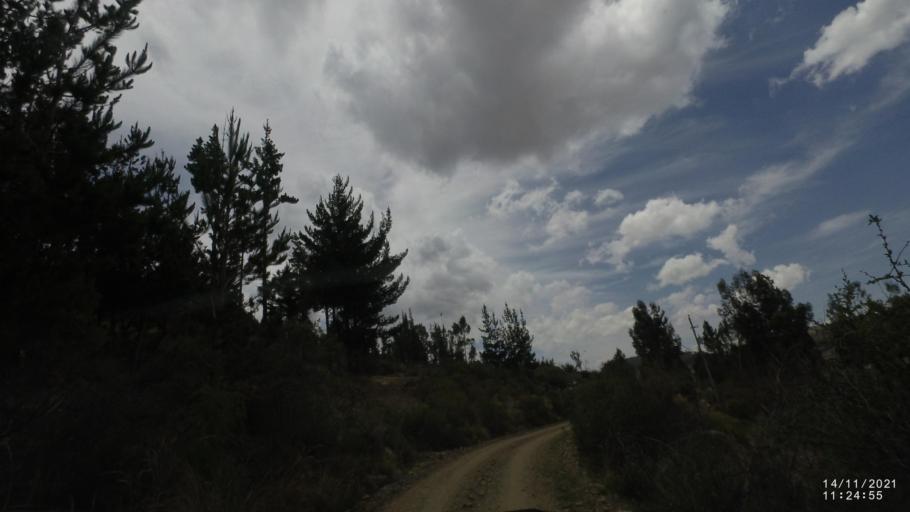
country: BO
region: Cochabamba
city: Cochabamba
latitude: -17.3346
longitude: -66.0241
